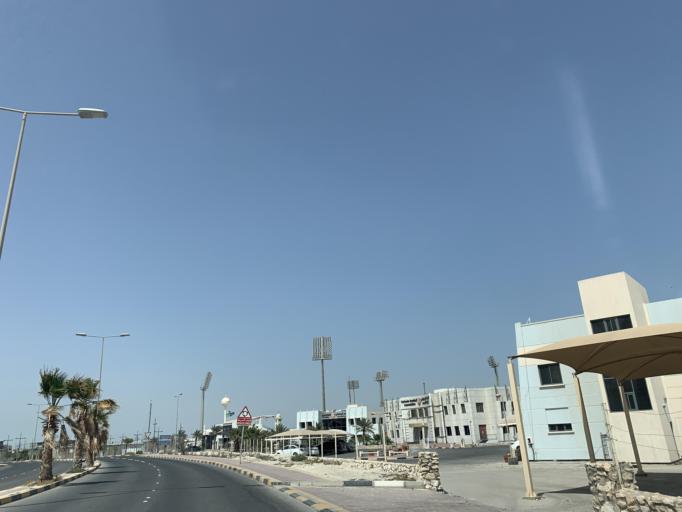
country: BH
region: Northern
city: Madinat `Isa
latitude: 26.1527
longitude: 50.5454
